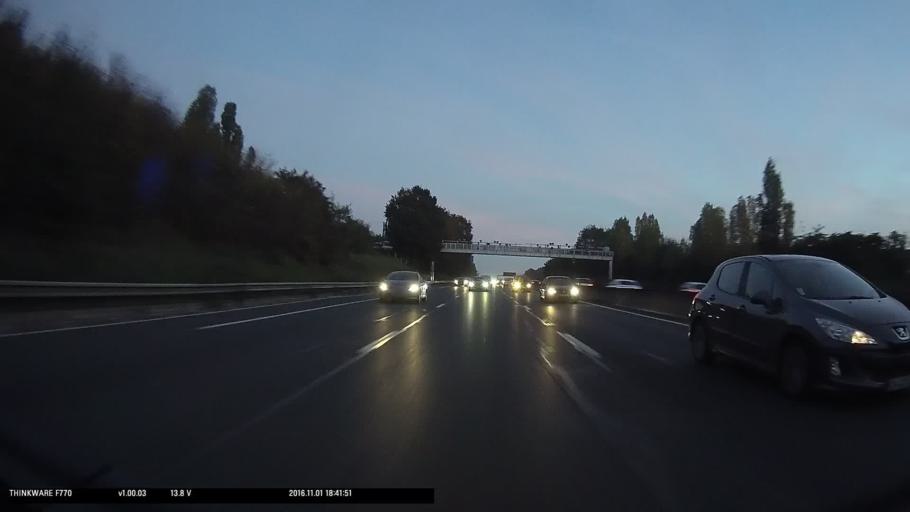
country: FR
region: Ile-de-France
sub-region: Departement de l'Essonne
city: Longjumeau
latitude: 48.6929
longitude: 2.3211
